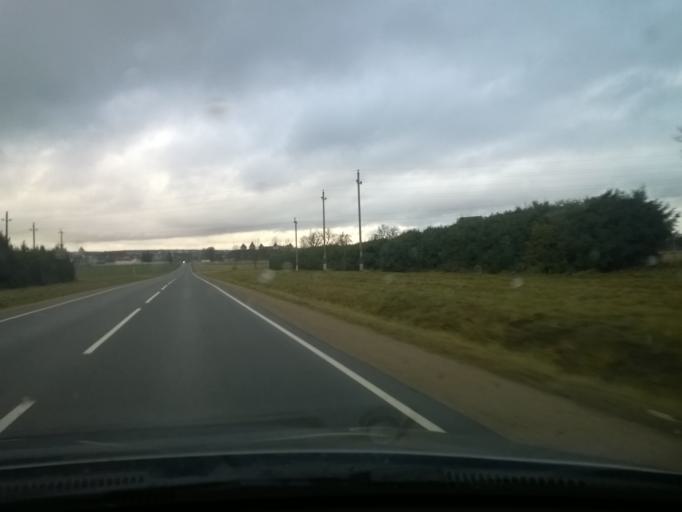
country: BY
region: Grodnenskaya
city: Mir
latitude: 53.4423
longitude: 26.4772
